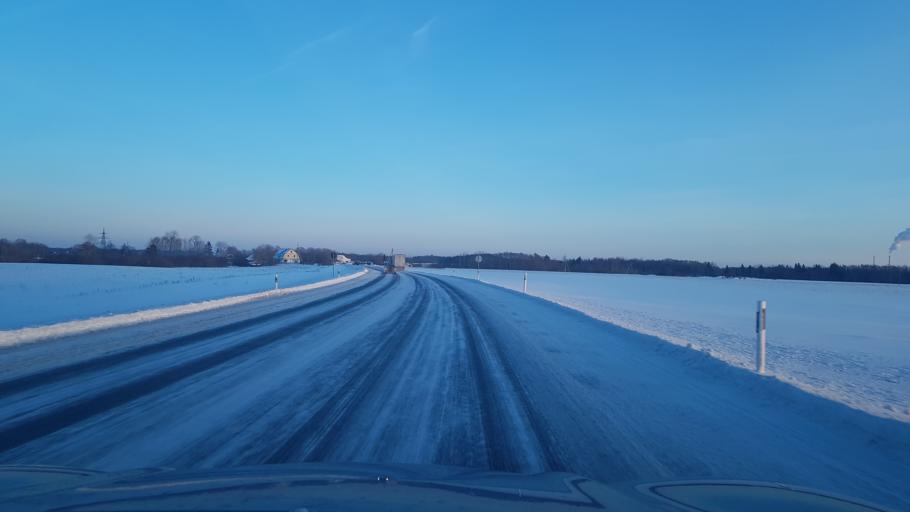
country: EE
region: Ida-Virumaa
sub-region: Narva-Joesuu linn
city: Narva-Joesuu
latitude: 59.4027
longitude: 28.0546
